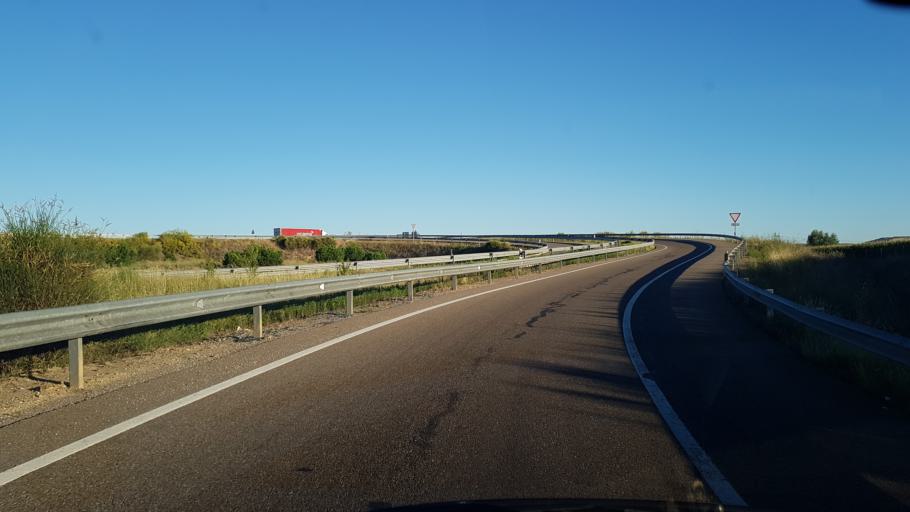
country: ES
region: Castille and Leon
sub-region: Provincia de Zamora
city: Monfarracinos
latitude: 41.5326
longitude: -5.7025
